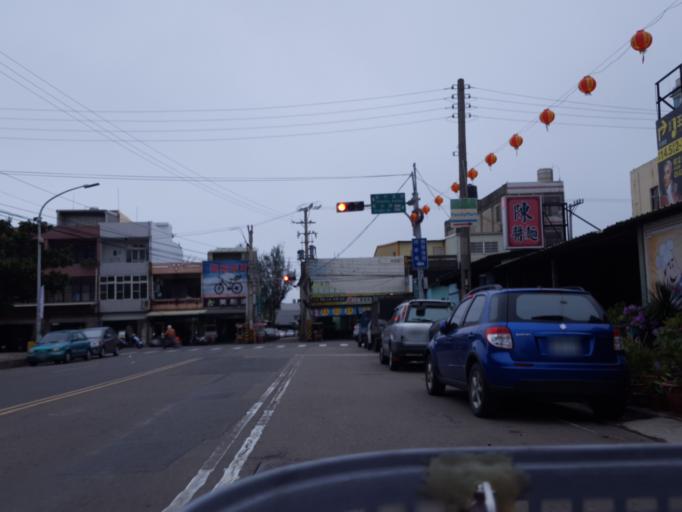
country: TW
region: Taiwan
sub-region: Hsinchu
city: Hsinchu
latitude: 24.8452
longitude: 120.9273
